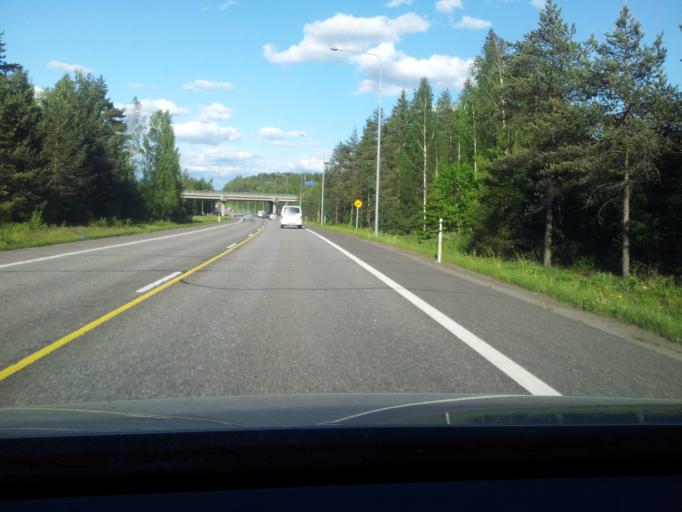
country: FI
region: Kymenlaakso
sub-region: Kouvola
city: Kouvola
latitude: 60.8847
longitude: 26.7619
